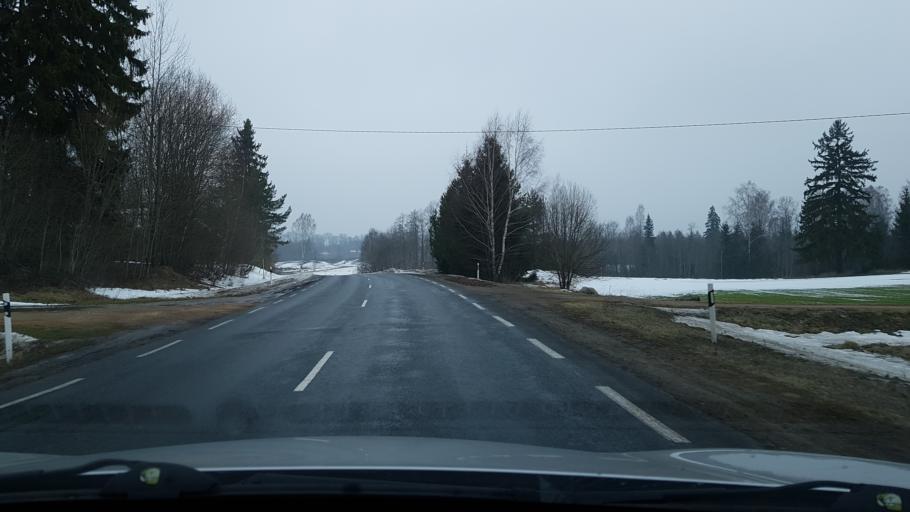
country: EE
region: Valgamaa
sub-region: Torva linn
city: Torva
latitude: 58.1414
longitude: 25.9865
